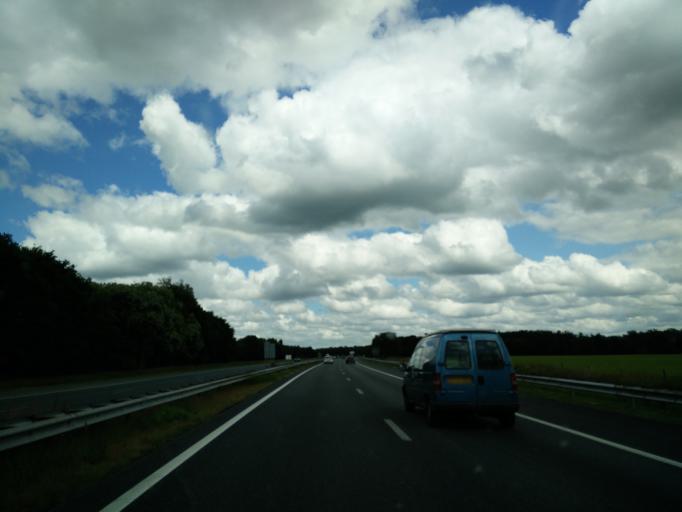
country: NL
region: Drenthe
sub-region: Gemeente Tynaarlo
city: Tynaarlo
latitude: 53.0903
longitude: 6.6065
